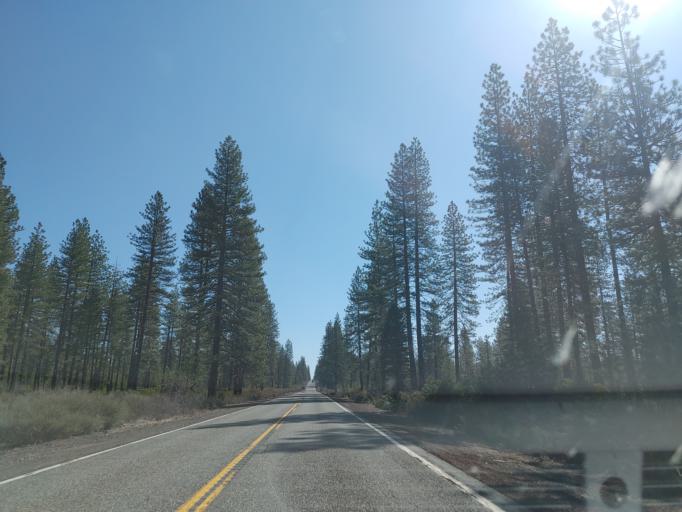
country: US
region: California
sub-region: Siskiyou County
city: McCloud
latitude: 41.2554
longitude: -122.0539
